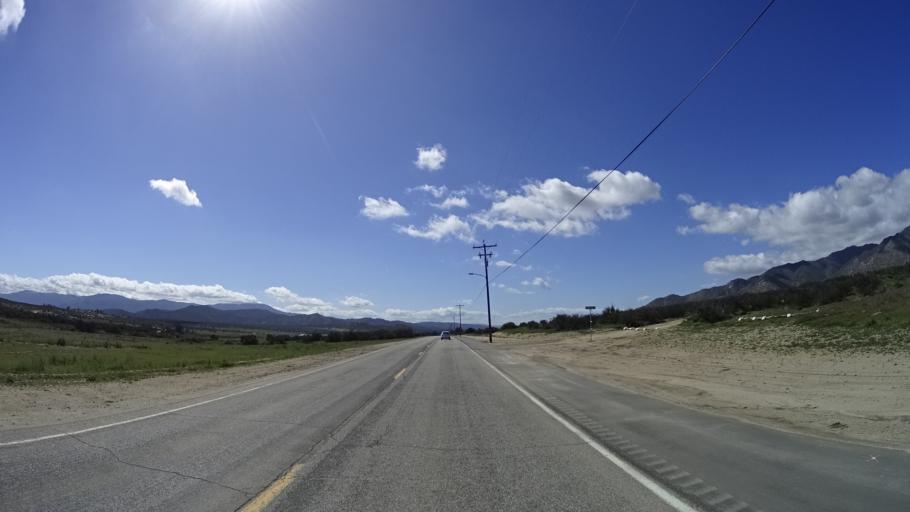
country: US
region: California
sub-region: San Diego County
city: Borrego Springs
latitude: 33.2105
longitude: -116.5096
